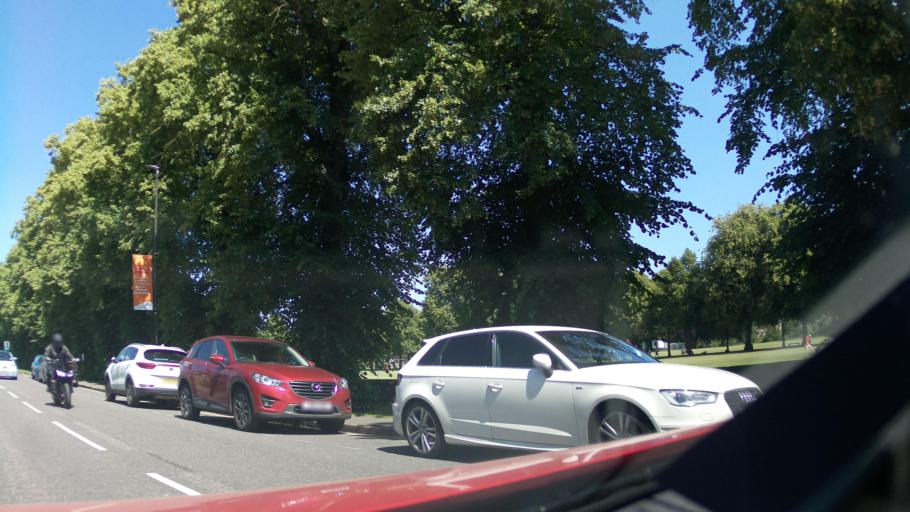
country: GB
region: England
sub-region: Derbyshire
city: Bakewell
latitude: 53.2089
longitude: -1.6710
